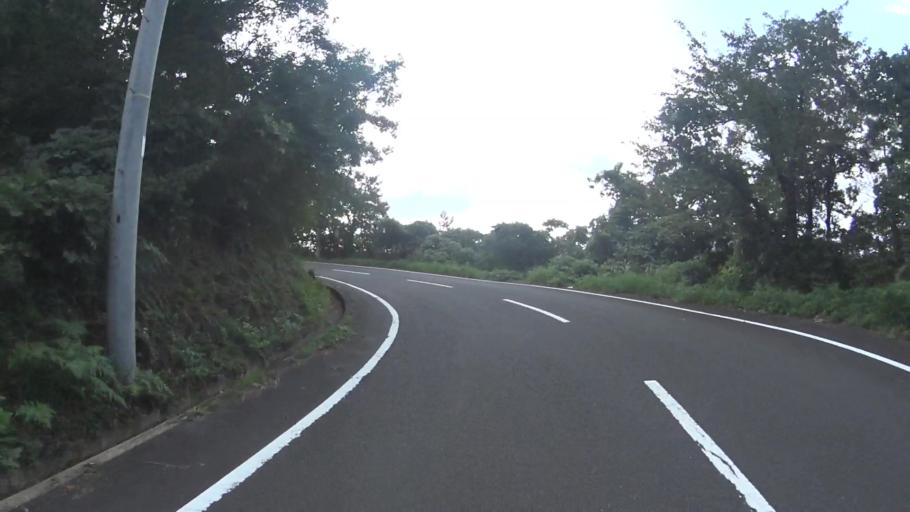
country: JP
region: Kyoto
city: Miyazu
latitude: 35.7407
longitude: 135.1752
